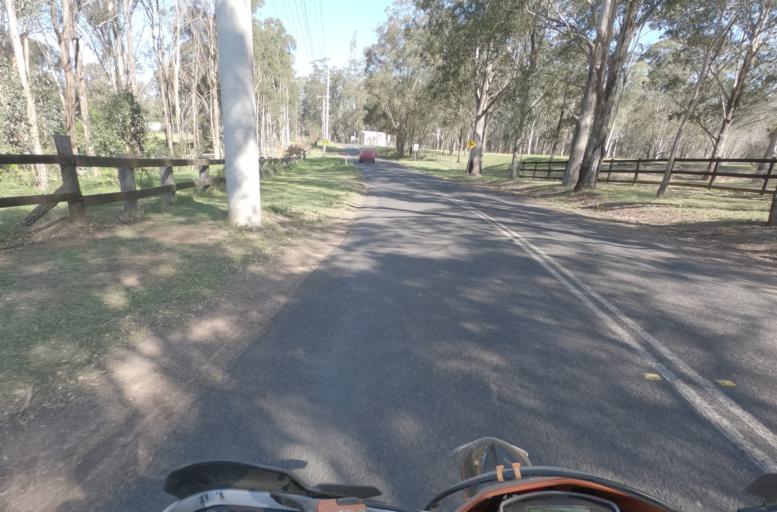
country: AU
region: New South Wales
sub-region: Hawkesbury
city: Scheyville
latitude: -33.5857
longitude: 150.9079
